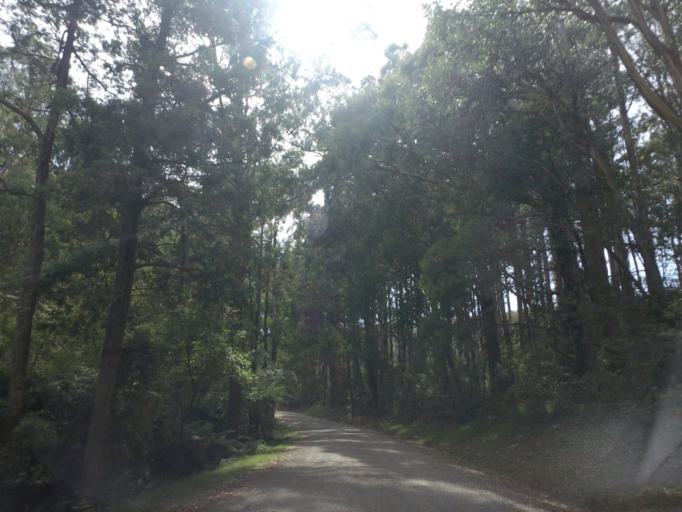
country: AU
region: Victoria
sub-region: Yarra Ranges
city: Healesville
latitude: -37.5552
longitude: 145.5122
